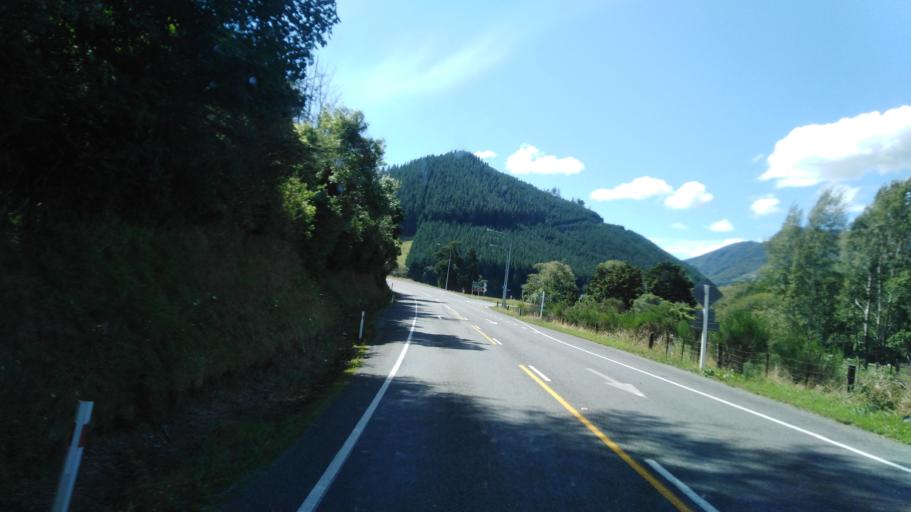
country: NZ
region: Nelson
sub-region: Nelson City
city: Nelson
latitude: -41.2199
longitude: 173.5861
